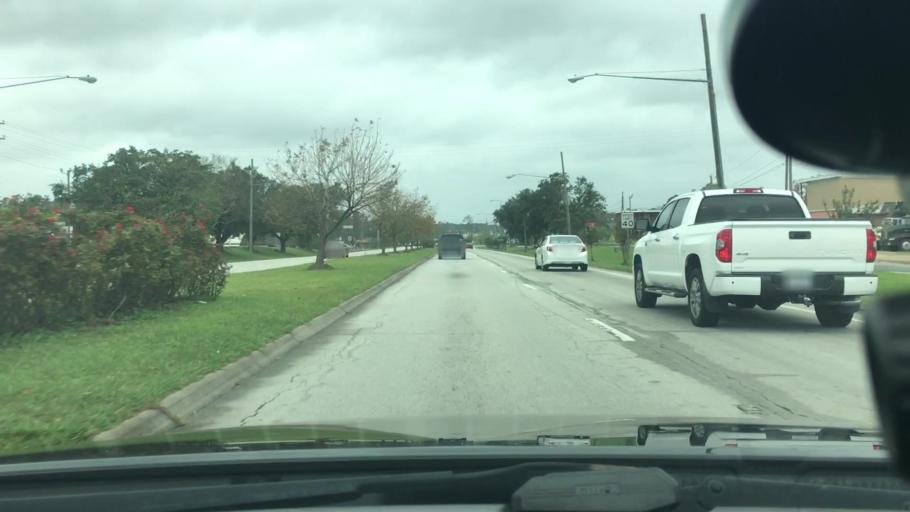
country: US
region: North Carolina
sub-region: Craven County
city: Havelock
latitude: 34.8875
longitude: -76.9175
